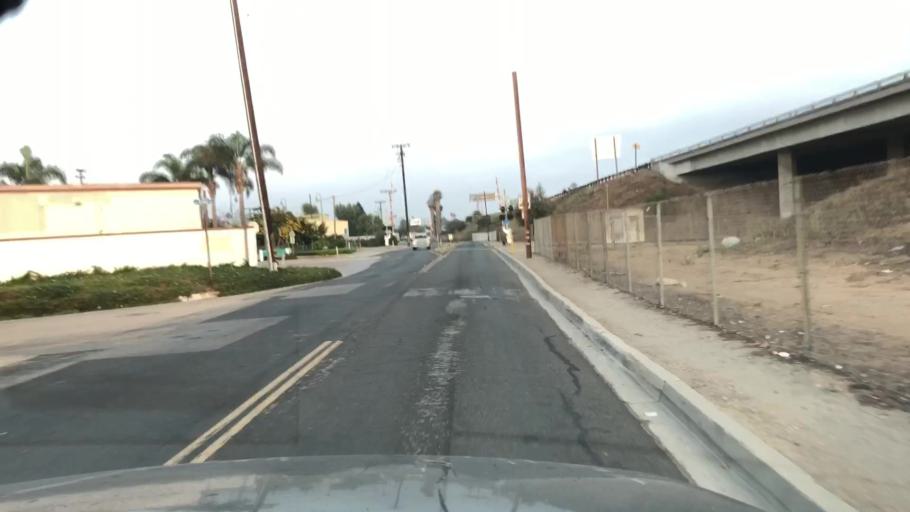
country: US
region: California
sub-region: Ventura County
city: El Rio
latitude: 34.2507
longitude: -119.2068
